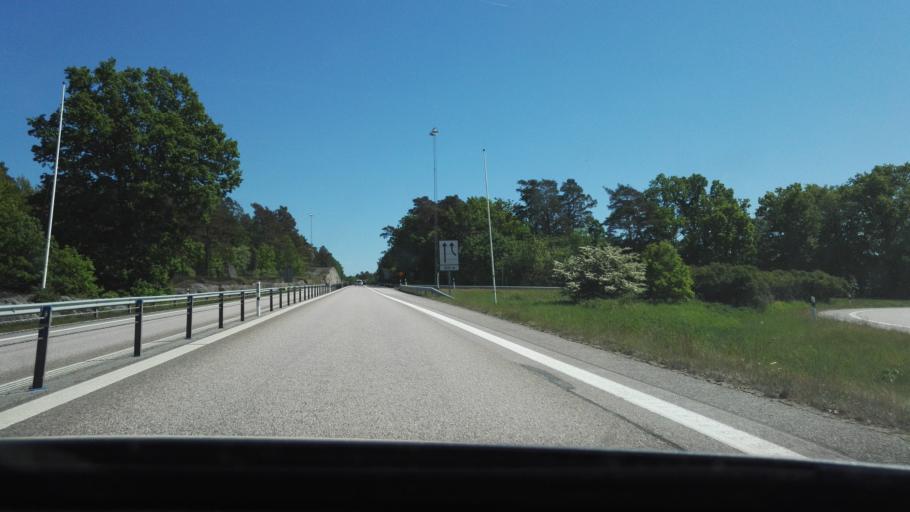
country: SE
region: Blekinge
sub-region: Ronneby Kommun
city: Kallinge
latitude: 56.2213
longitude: 15.2819
